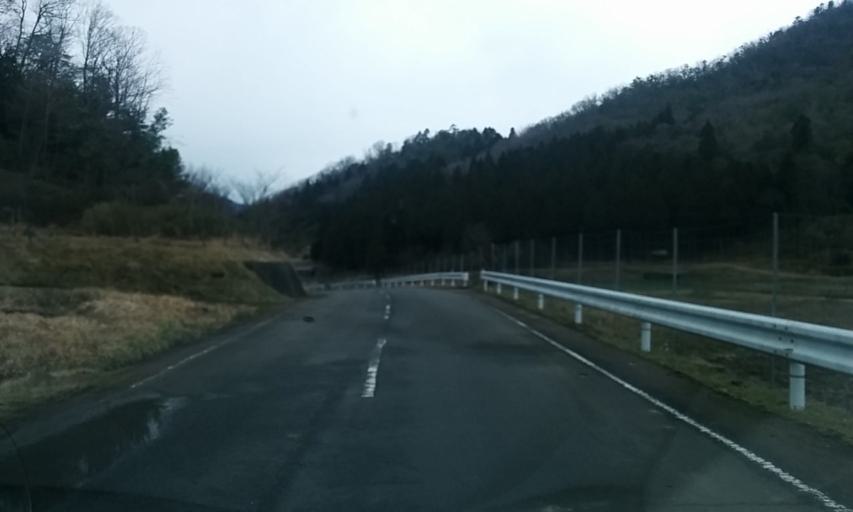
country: JP
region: Kyoto
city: Kameoka
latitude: 35.1186
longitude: 135.4208
